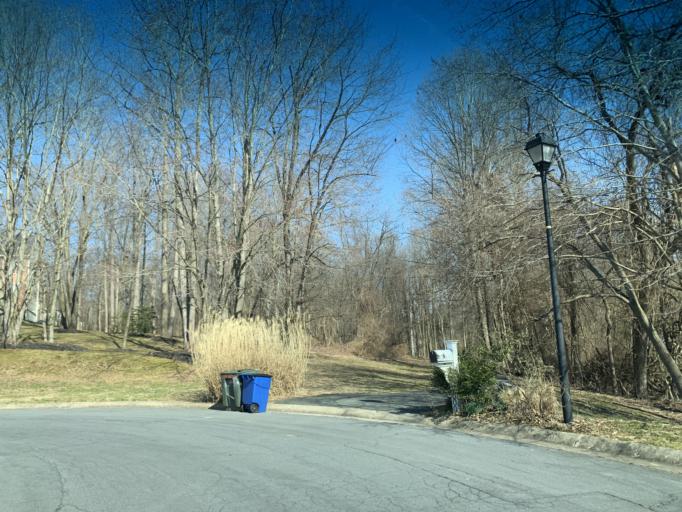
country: US
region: Maryland
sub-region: Harford County
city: Fallston
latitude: 39.5150
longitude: -76.4324
